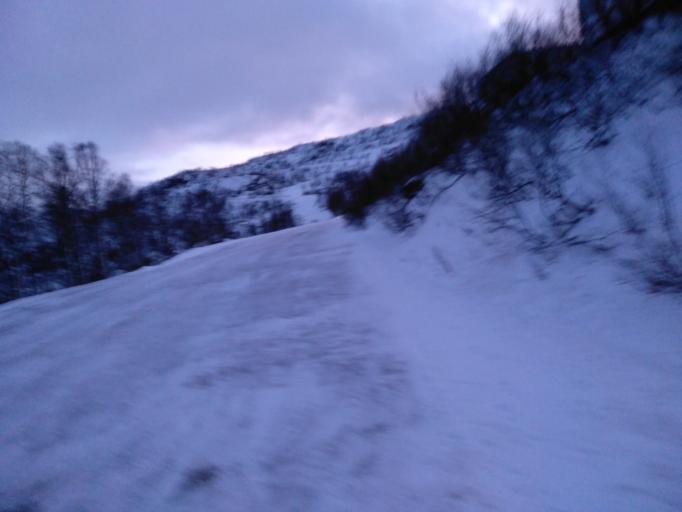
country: NO
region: Vest-Agder
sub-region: Sirdal
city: Tonstad
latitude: 59.0211
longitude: 6.9224
